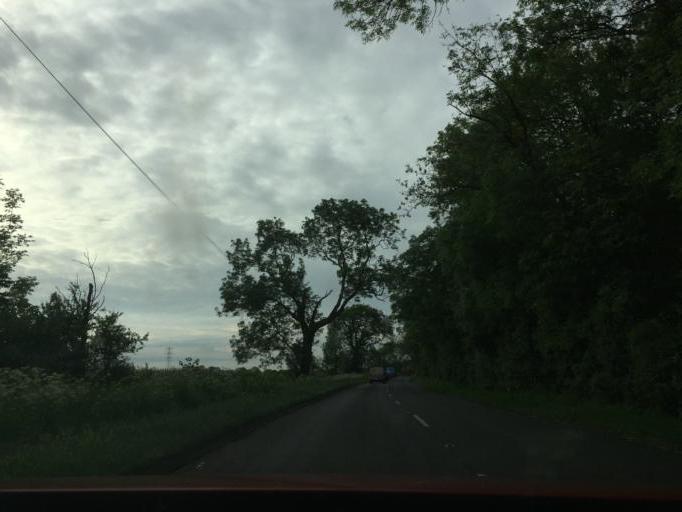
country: GB
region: England
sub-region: Leicestershire
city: Sapcote
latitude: 52.4644
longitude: -1.2996
